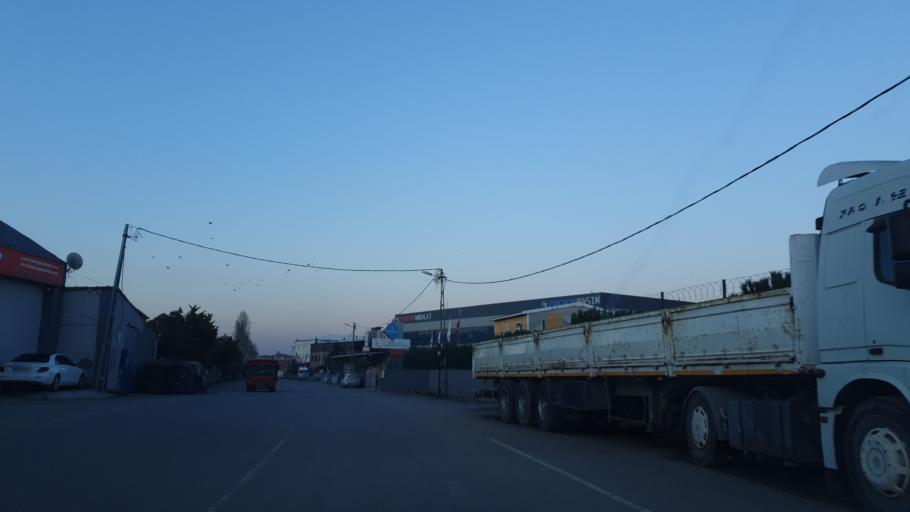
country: TR
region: Istanbul
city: Pendik
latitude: 40.8992
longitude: 29.2936
